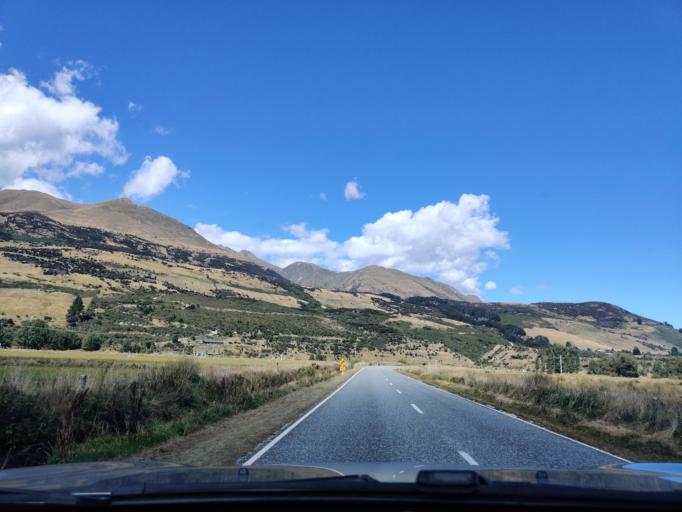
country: NZ
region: Otago
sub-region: Queenstown-Lakes District
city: Queenstown
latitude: -44.7924
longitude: 168.4013
